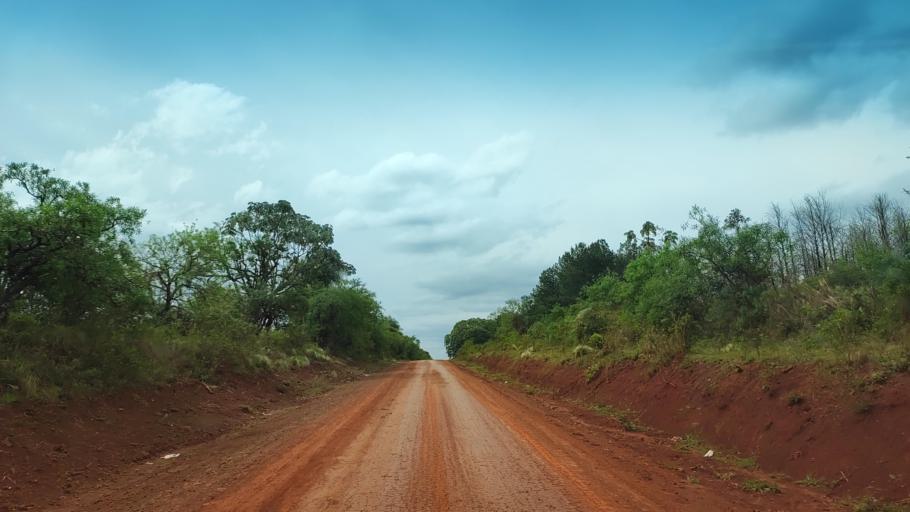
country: AR
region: Misiones
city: Garupa
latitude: -27.5142
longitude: -55.9707
